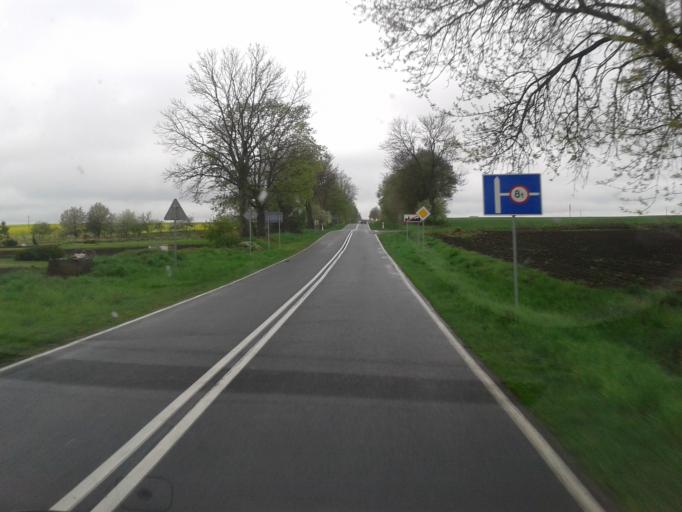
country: PL
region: Lublin Voivodeship
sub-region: Powiat tomaszowski
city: Telatyn
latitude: 50.5530
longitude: 23.9339
